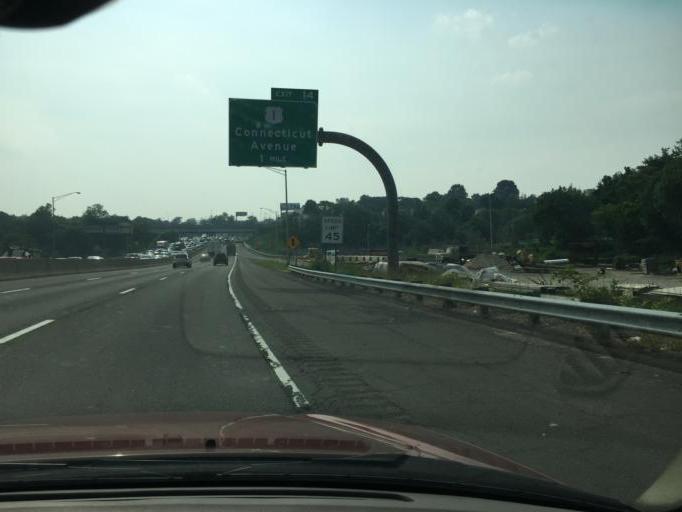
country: US
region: Connecticut
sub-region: Fairfield County
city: Norwalk
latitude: 41.1066
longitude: -73.4161
